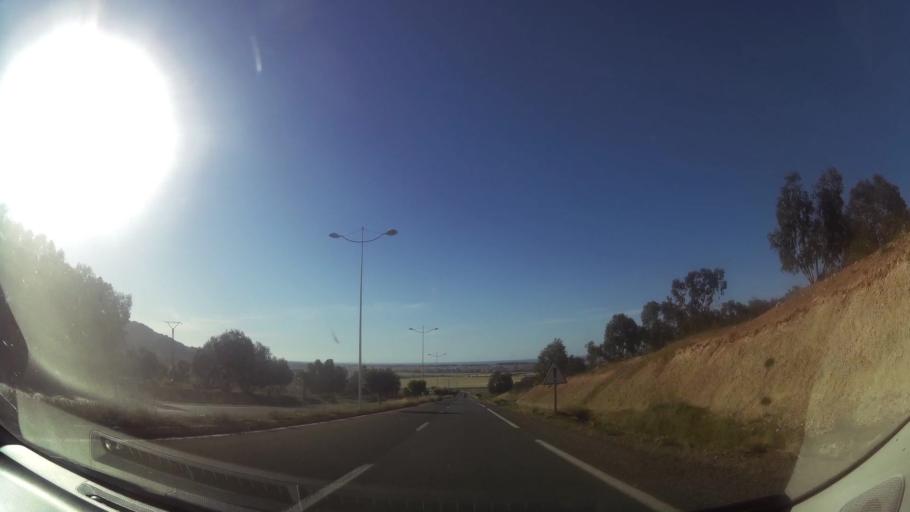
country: MA
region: Oriental
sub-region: Berkane-Taourirt
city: Madagh
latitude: 35.0590
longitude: -2.2222
